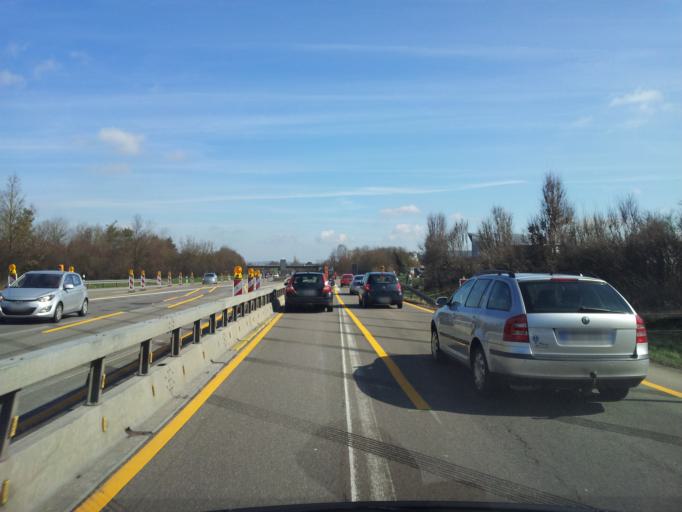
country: DE
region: Baden-Wuerttemberg
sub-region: Freiburg Region
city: Vohringen
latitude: 48.3119
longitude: 8.6416
